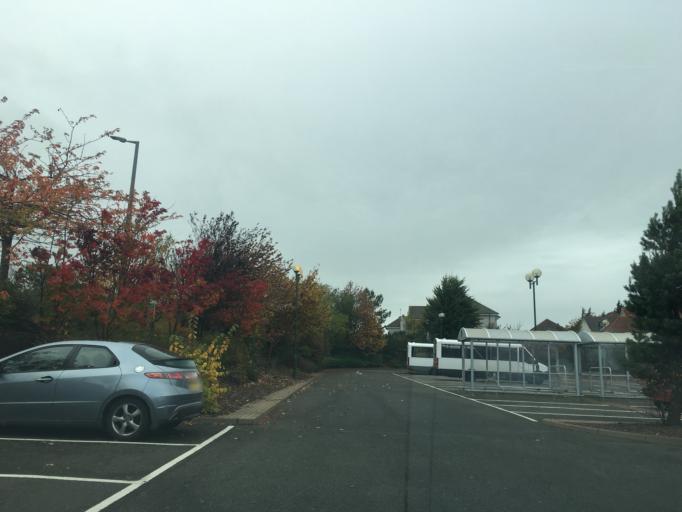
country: GB
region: Scotland
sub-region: Edinburgh
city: Colinton
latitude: 55.9014
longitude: -3.2243
